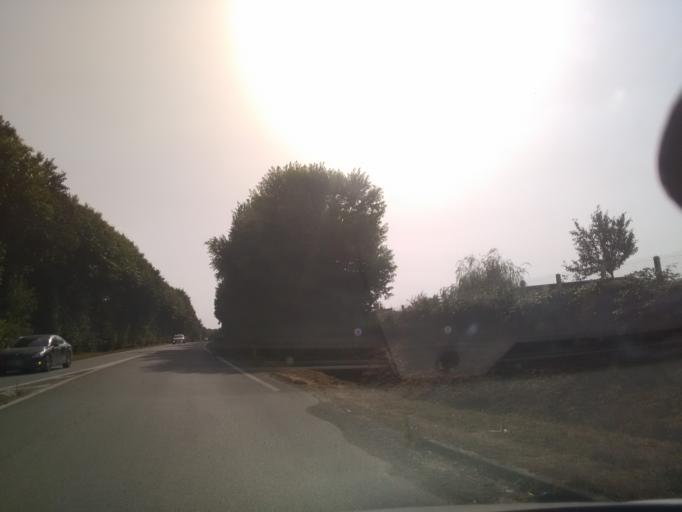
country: FR
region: Brittany
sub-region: Departement d'Ille-et-Vilaine
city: Hede-Bazouges
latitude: 48.3002
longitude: -1.8151
